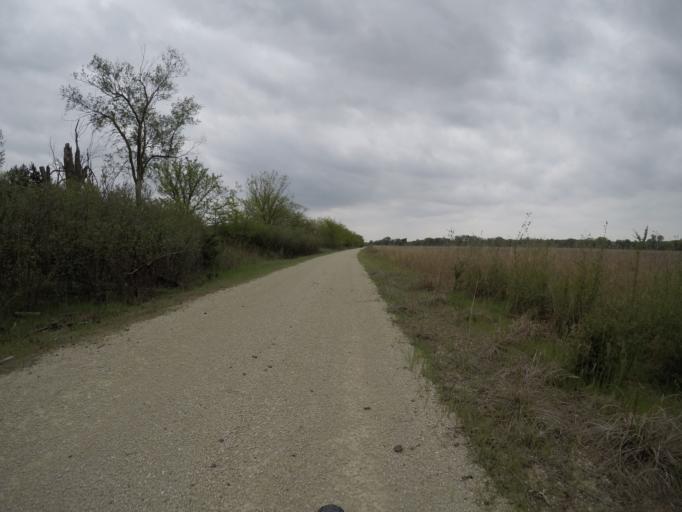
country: US
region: Nebraska
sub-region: Gage County
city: Wymore
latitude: 40.1211
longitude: -96.6369
